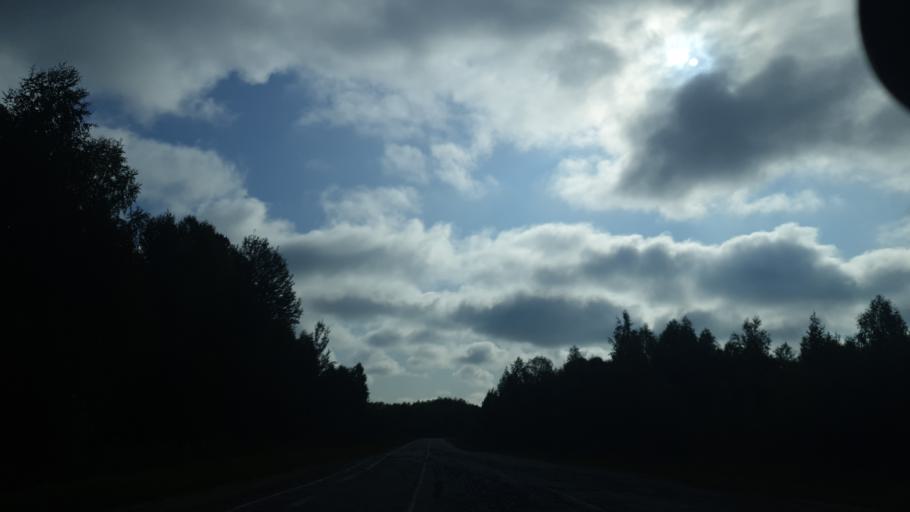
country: RU
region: Komi Republic
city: Vizinga
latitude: 60.6101
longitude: 50.4229
